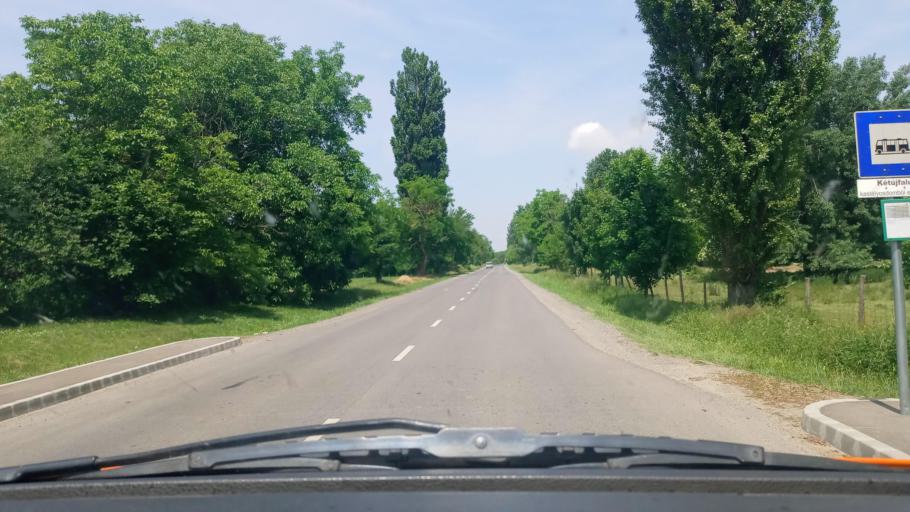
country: HU
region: Baranya
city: Szigetvar
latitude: 45.9669
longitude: 17.7230
